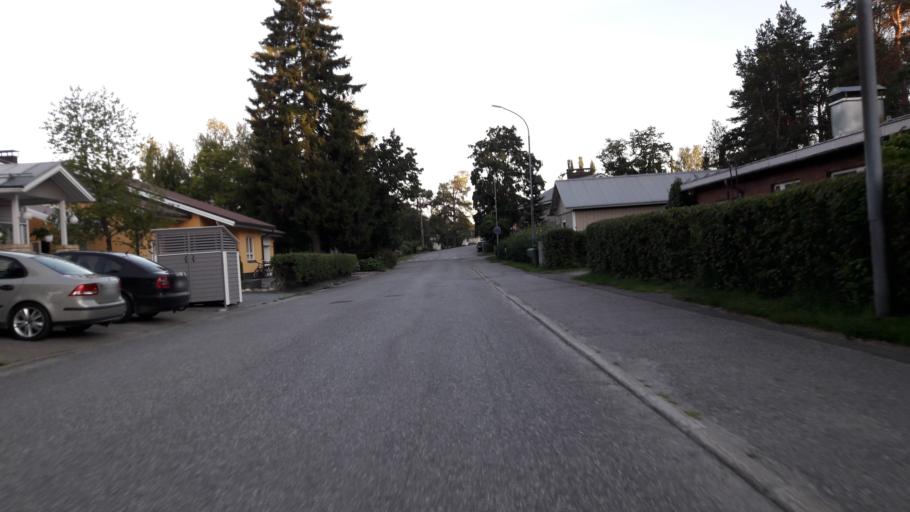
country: FI
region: North Karelia
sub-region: Joensuu
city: Joensuu
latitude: 62.6119
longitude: 29.7836
